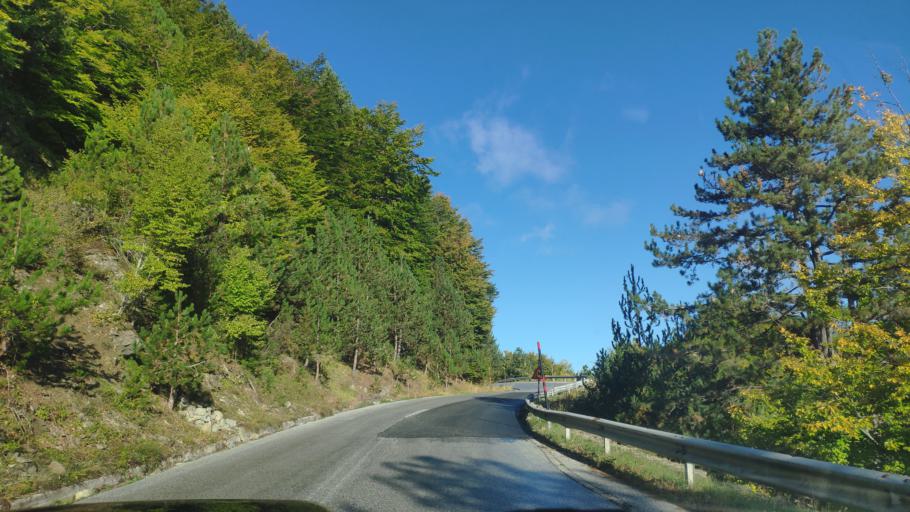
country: GR
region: Epirus
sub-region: Nomos Ioanninon
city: Metsovo
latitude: 39.7764
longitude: 21.1755
